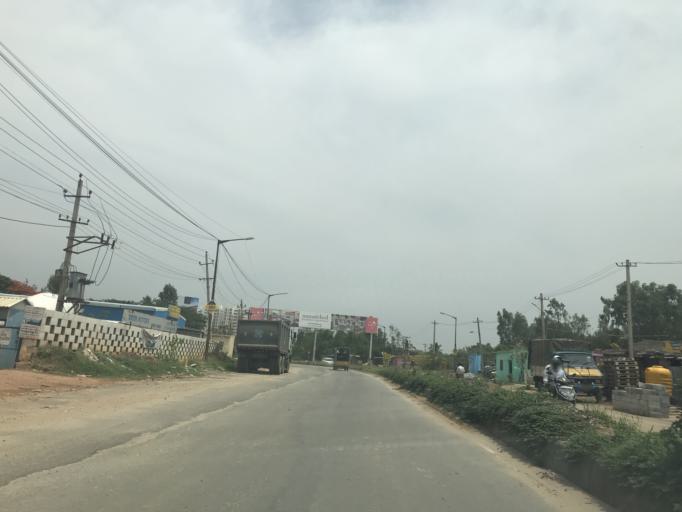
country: IN
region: Karnataka
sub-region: Bangalore Urban
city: Yelahanka
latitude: 13.0908
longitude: 77.6546
